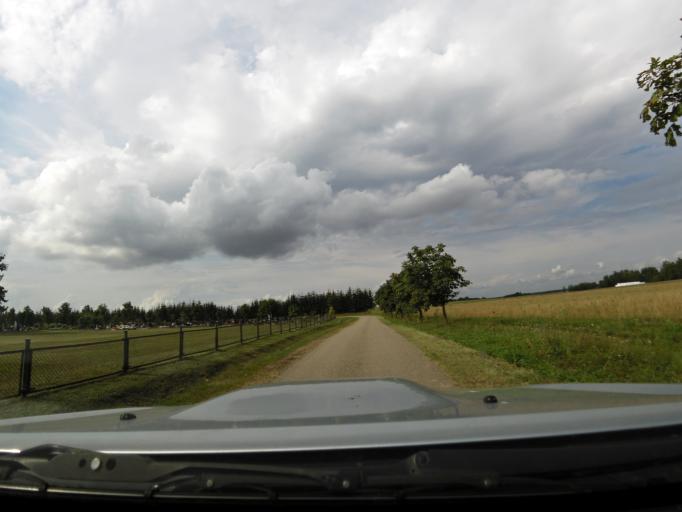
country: LT
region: Vilnius County
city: Elektrenai
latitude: 54.9121
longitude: 24.7244
